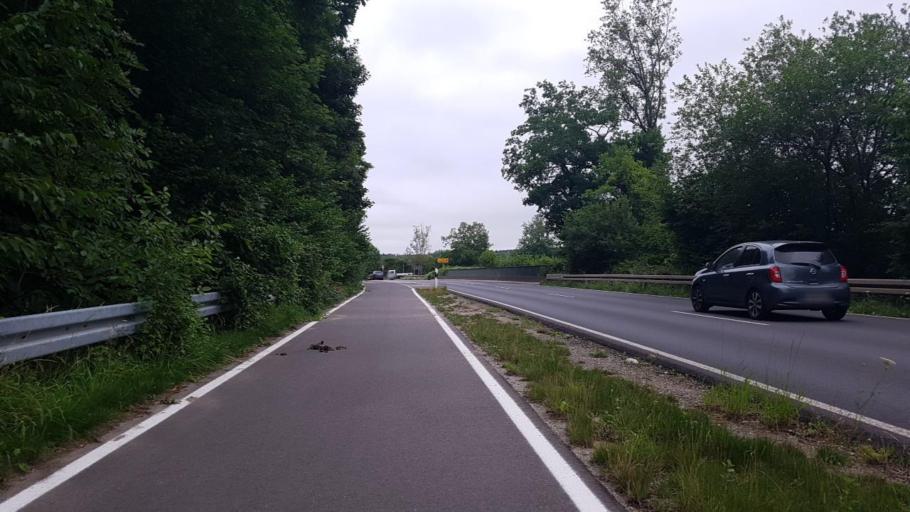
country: DE
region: North Rhine-Westphalia
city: Stolberg
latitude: 50.7893
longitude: 6.1776
